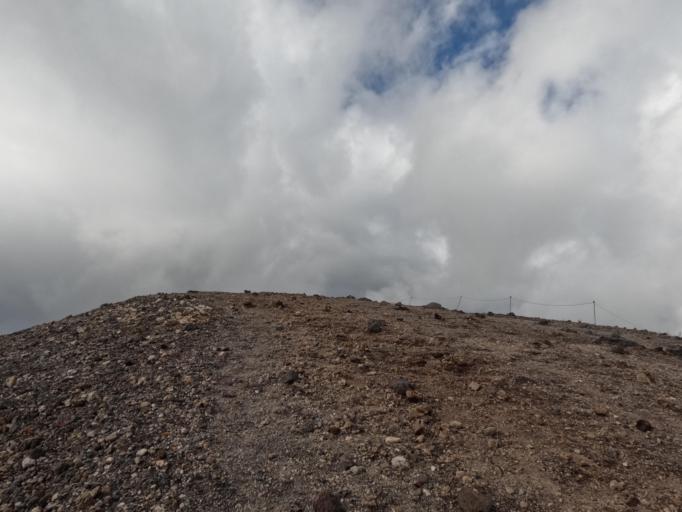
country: JP
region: Hokkaido
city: Shiraoi
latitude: 42.6912
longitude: 141.3870
